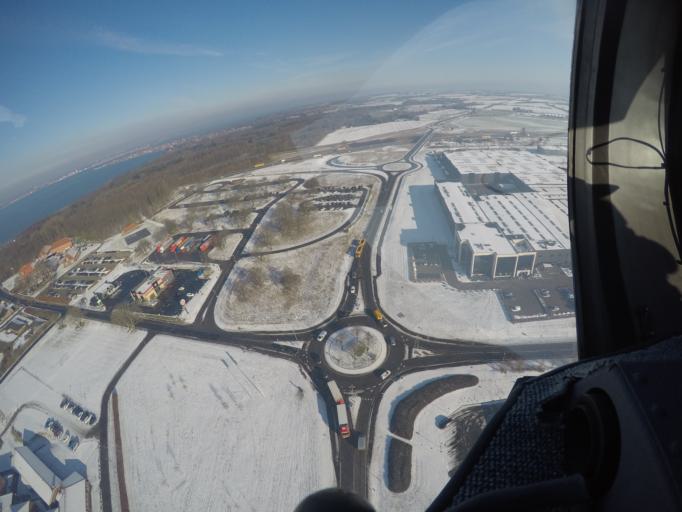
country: DK
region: South Denmark
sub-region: Middelfart Kommune
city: Strib
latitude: 55.5102
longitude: 9.7671
